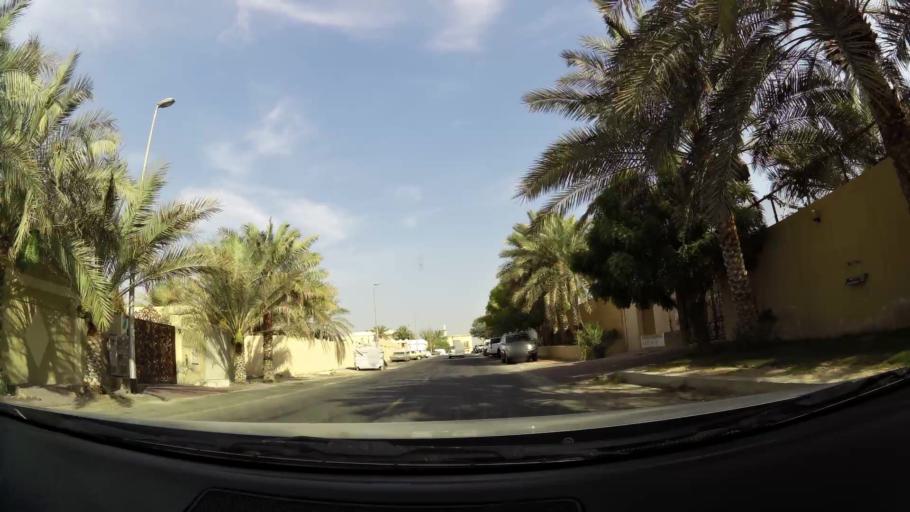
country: AE
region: Ash Shariqah
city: Sharjah
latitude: 25.2248
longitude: 55.3999
